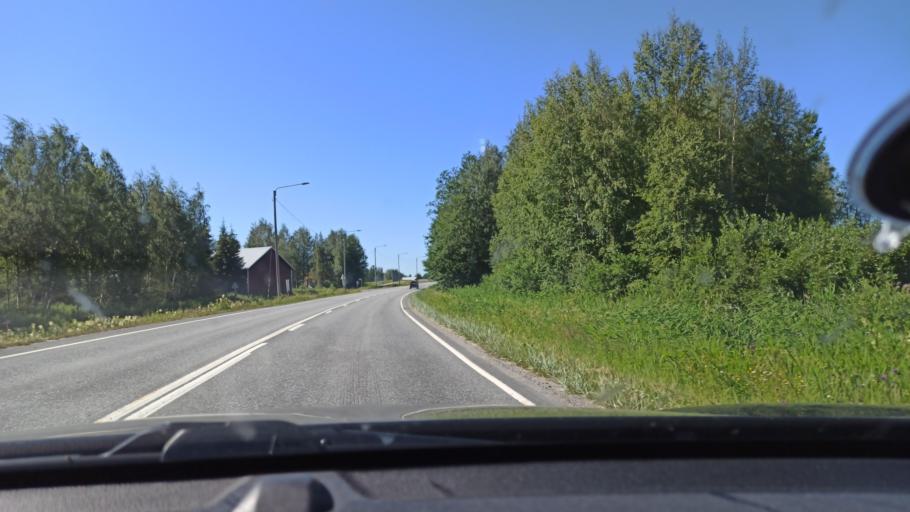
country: FI
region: Ostrobothnia
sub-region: Jakobstadsregionen
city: Bennaes
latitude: 63.6083
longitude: 22.7745
